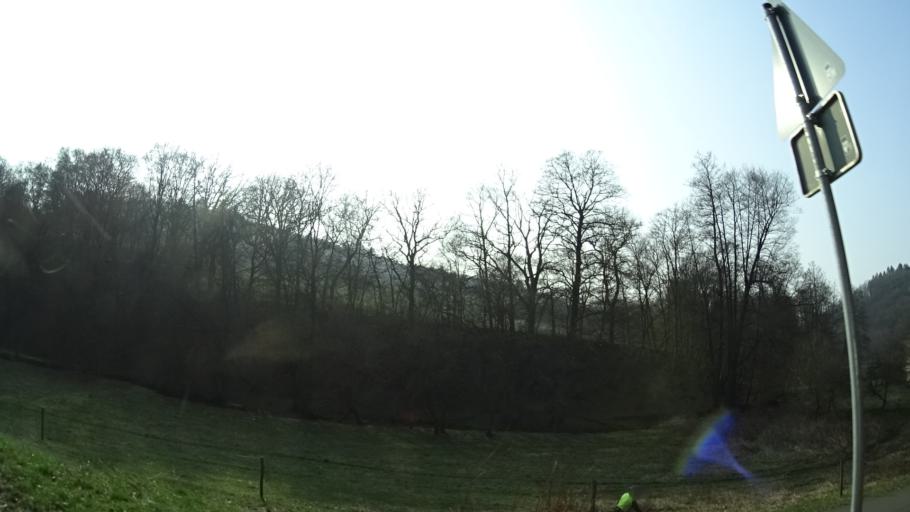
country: DE
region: Rheinland-Pfalz
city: Fockelberg
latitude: 49.5481
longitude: 7.4867
